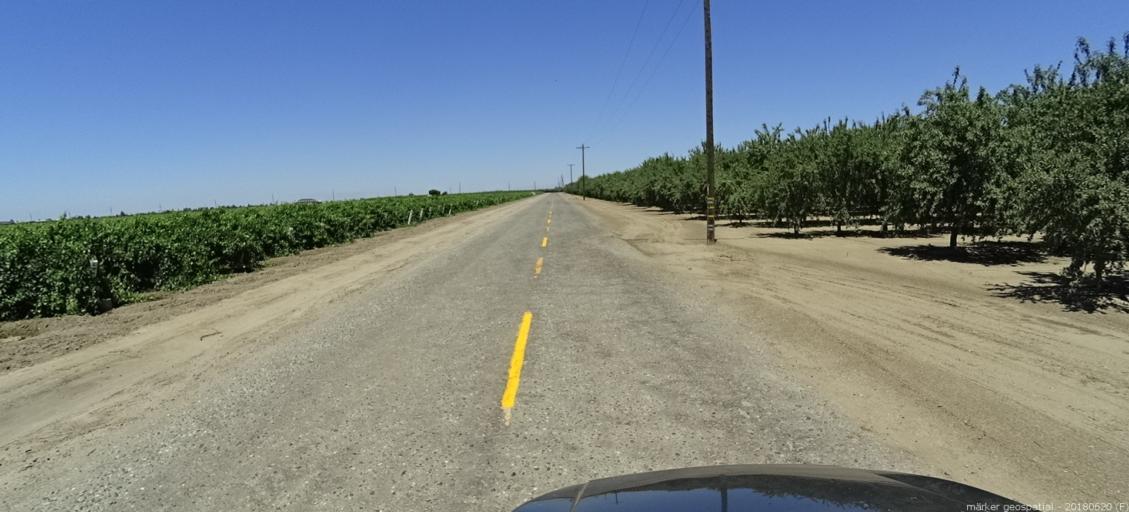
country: US
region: California
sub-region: Madera County
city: Parkwood
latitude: 36.9173
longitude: -120.0375
